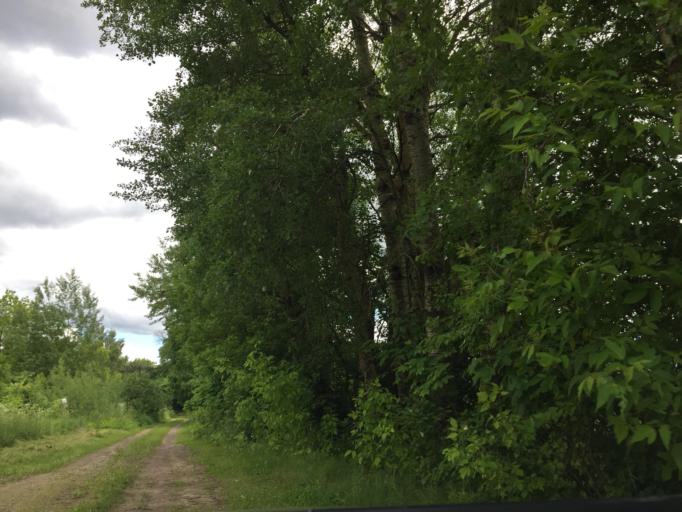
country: LV
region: Garkalne
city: Garkalne
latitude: 57.0739
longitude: 24.4002
